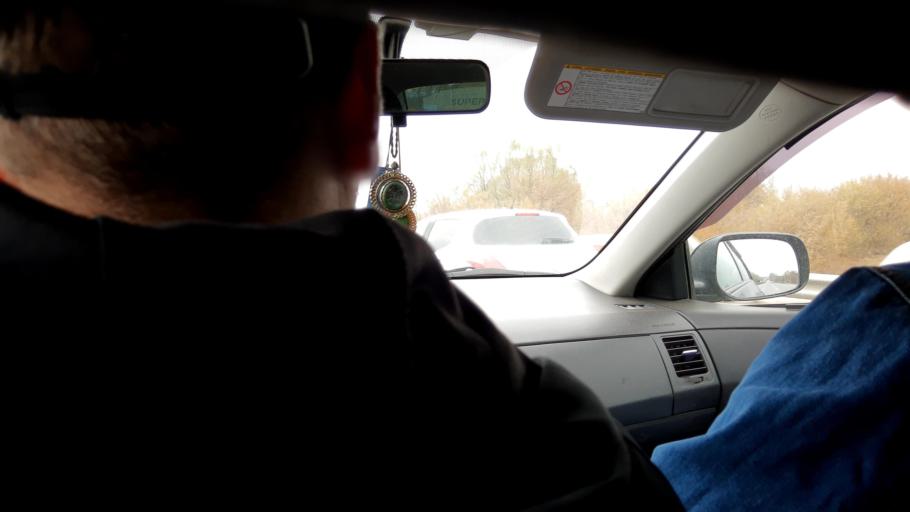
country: RU
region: Bashkortostan
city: Ufa
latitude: 54.5177
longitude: 55.9025
